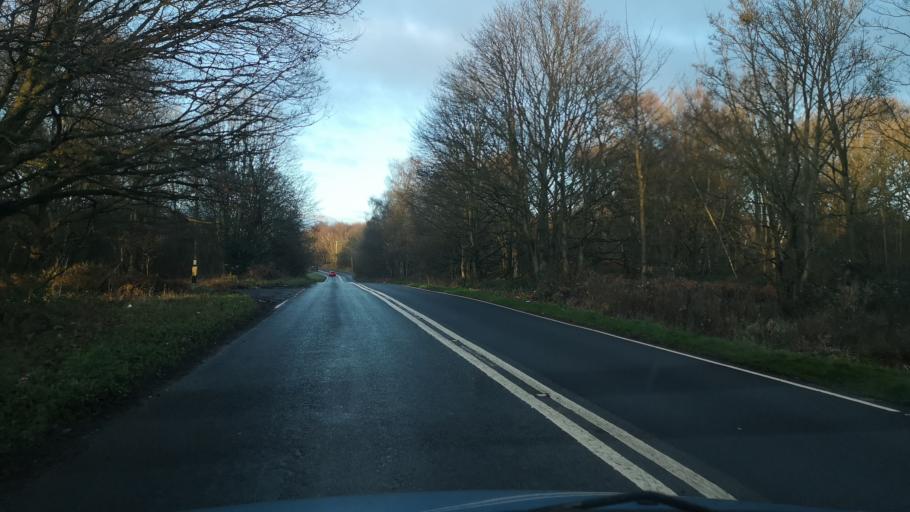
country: GB
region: England
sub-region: Barnsley
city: Great Houghton
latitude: 53.5692
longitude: -1.3499
